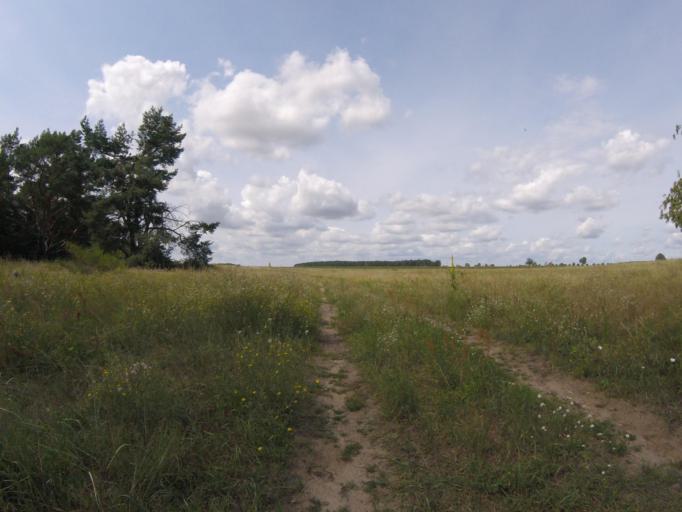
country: DE
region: Brandenburg
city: Mittenwalde
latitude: 52.2769
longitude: 13.5045
